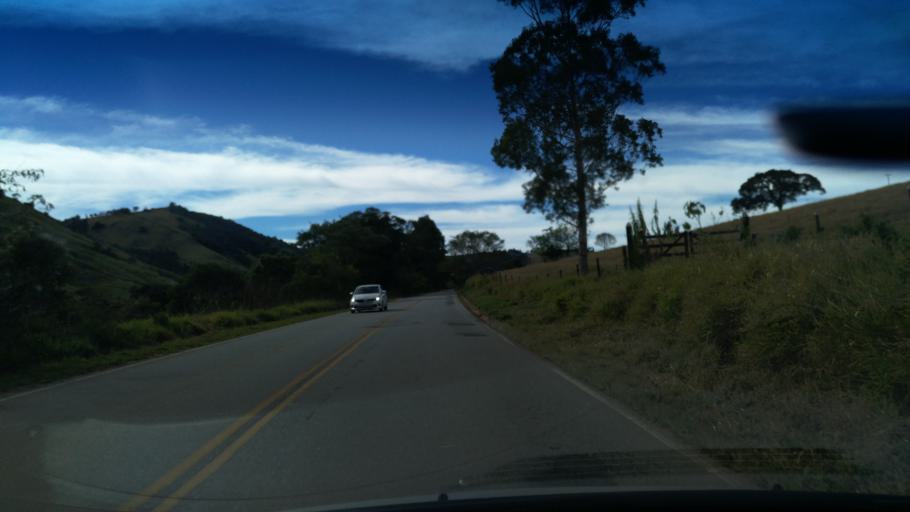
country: BR
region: Minas Gerais
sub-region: Andradas
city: Andradas
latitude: -22.0540
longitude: -46.4052
